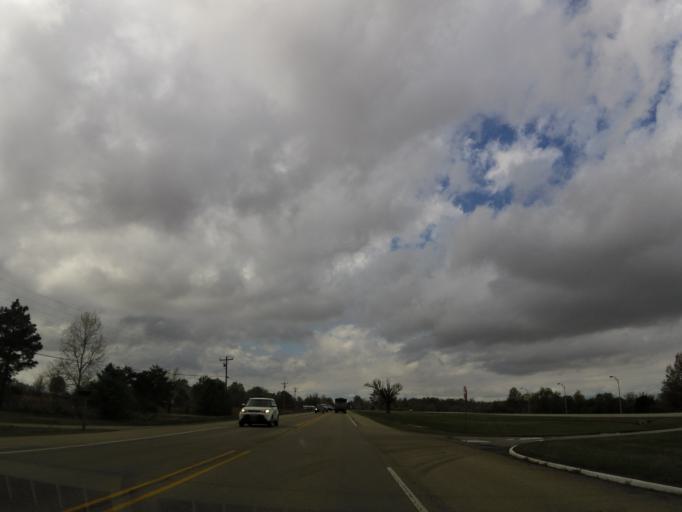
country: US
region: Arkansas
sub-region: Clay County
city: Corning
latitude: 36.4807
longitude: -90.5506
